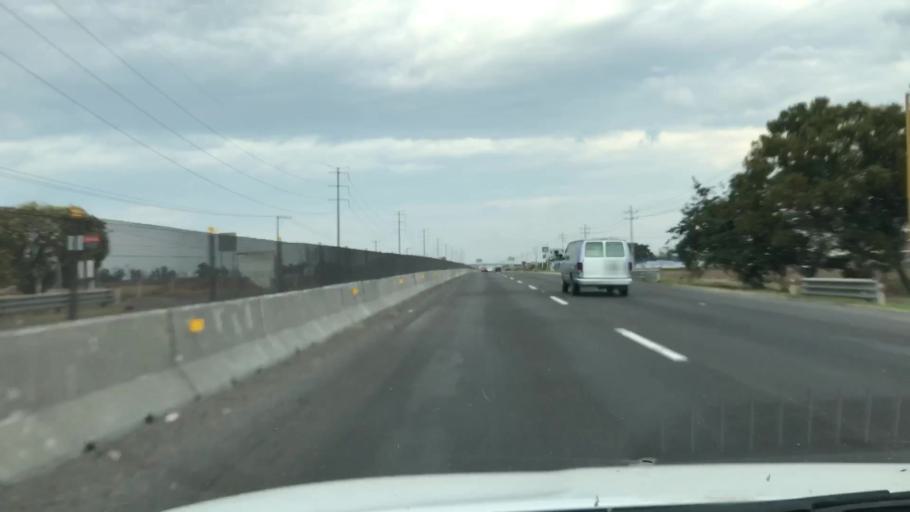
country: MX
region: Guanajuato
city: Salamanca
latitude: 20.5686
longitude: -101.2250
